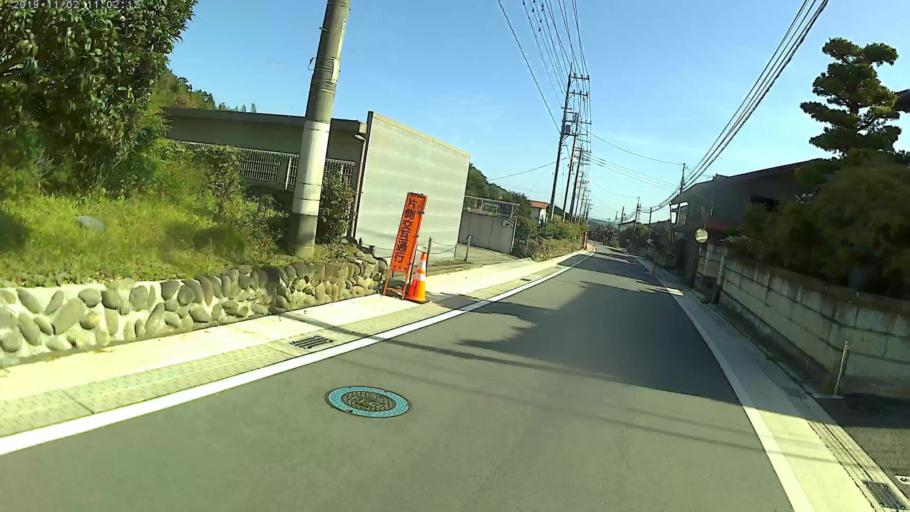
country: JP
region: Gunma
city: Annaka
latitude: 36.3063
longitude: 138.8301
